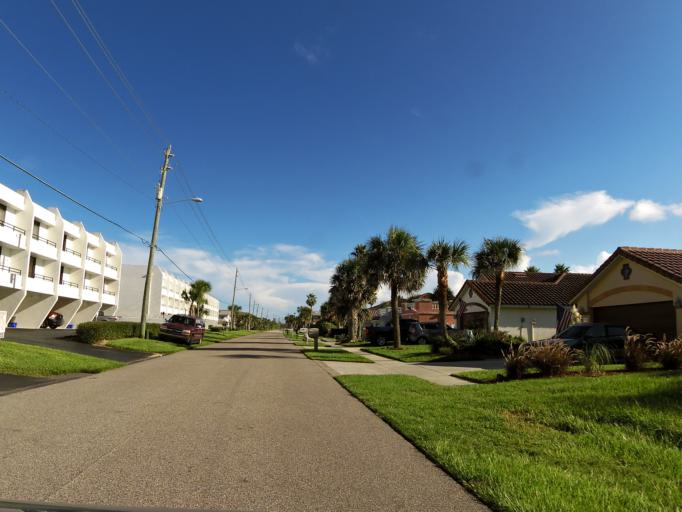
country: US
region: Florida
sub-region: Flagler County
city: Flagler Beach
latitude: 29.4939
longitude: -81.1343
